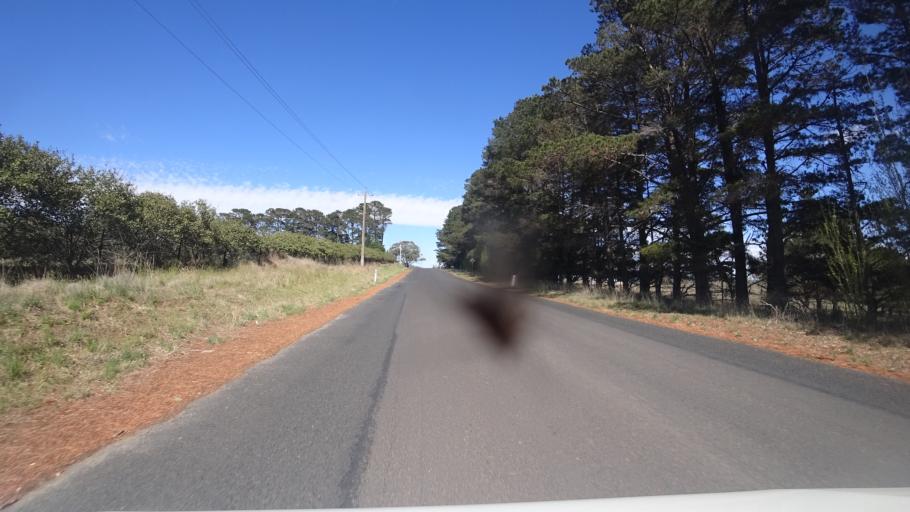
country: AU
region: New South Wales
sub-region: Lithgow
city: Bowenfels
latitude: -33.5172
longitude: 149.9898
